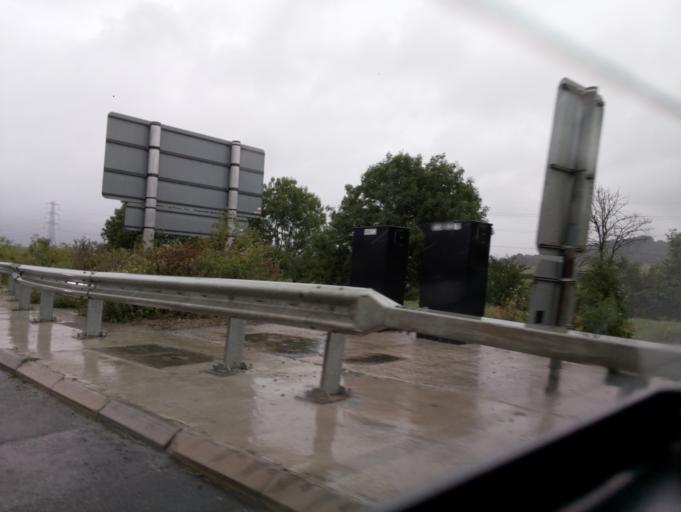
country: GB
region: England
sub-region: Gloucestershire
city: Barnwood
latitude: 51.8680
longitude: -2.1964
